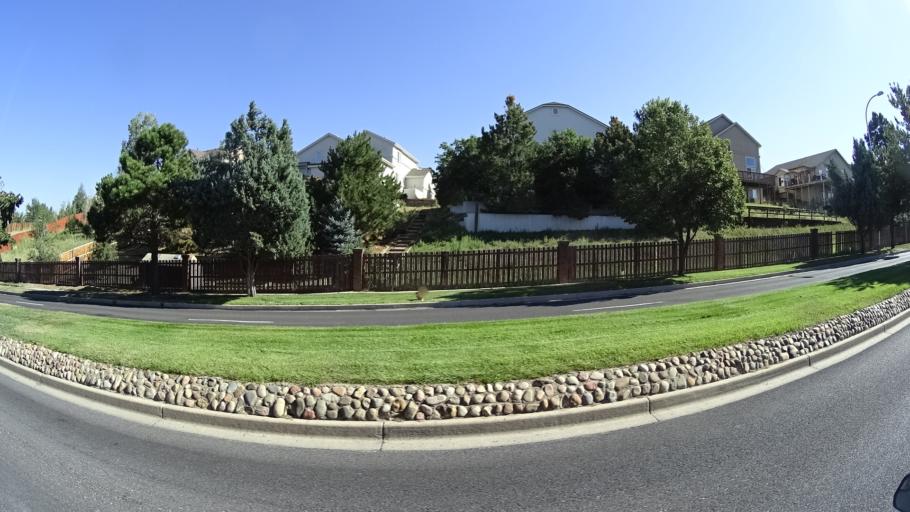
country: US
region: Colorado
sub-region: El Paso County
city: Cimarron Hills
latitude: 38.9223
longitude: -104.7448
